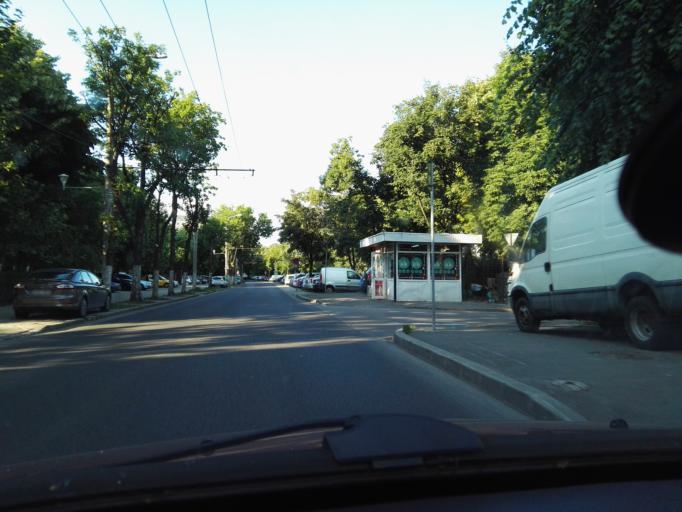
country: RO
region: Bucuresti
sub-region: Municipiul Bucuresti
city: Bucuresti
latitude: 44.3859
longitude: 26.1026
